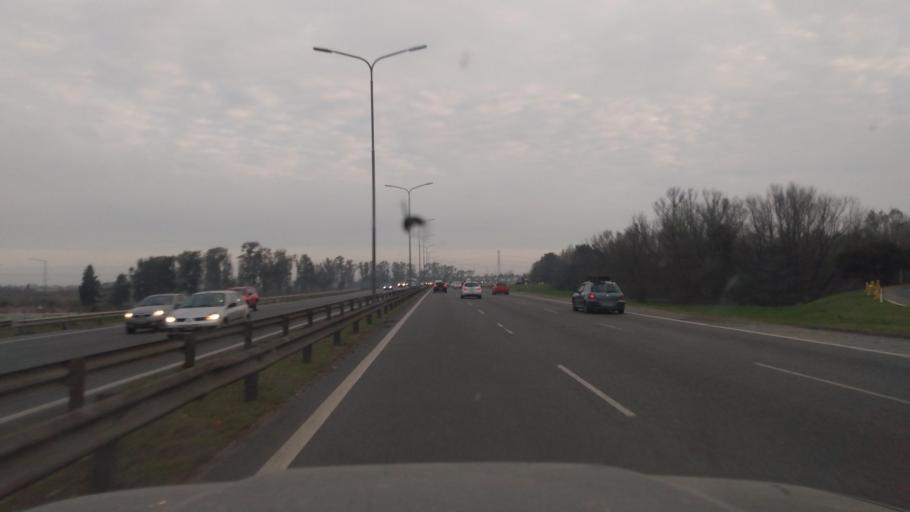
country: AR
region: Buenos Aires
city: Hurlingham
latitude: -34.5444
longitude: -58.6028
